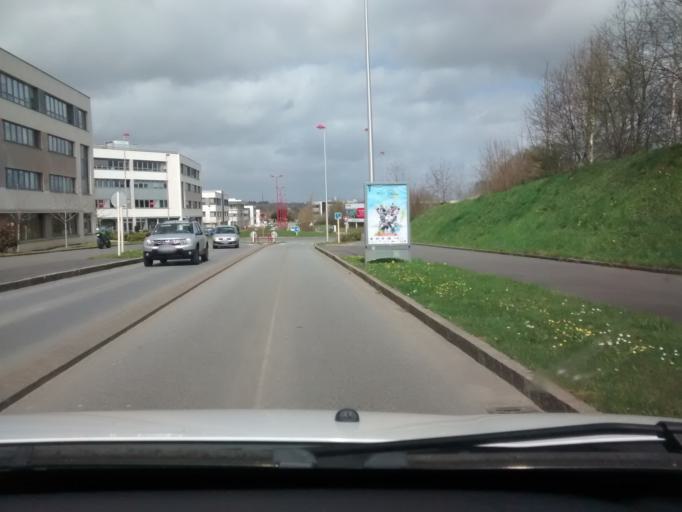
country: FR
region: Brittany
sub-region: Departement d'Ille-et-Vilaine
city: Saint-Gregoire
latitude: 48.1511
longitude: -1.6972
